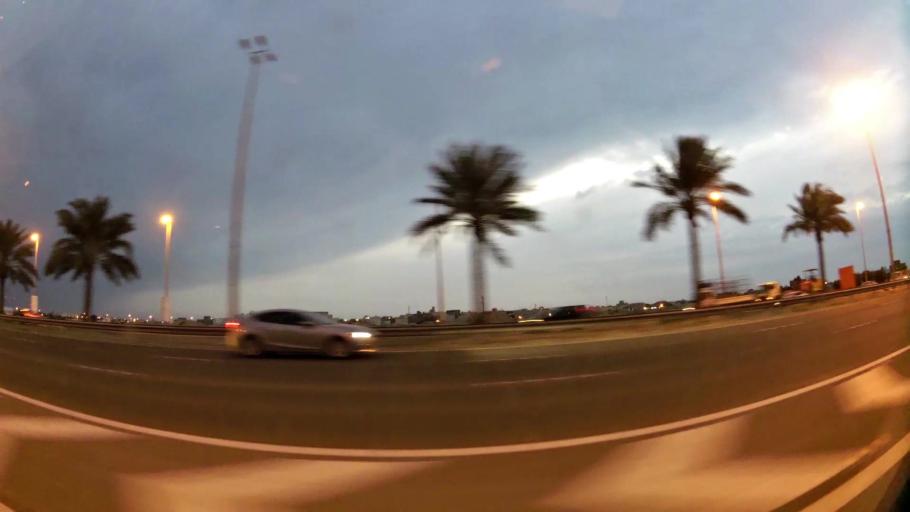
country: BH
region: Central Governorate
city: Madinat Hamad
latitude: 26.1466
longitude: 50.5097
